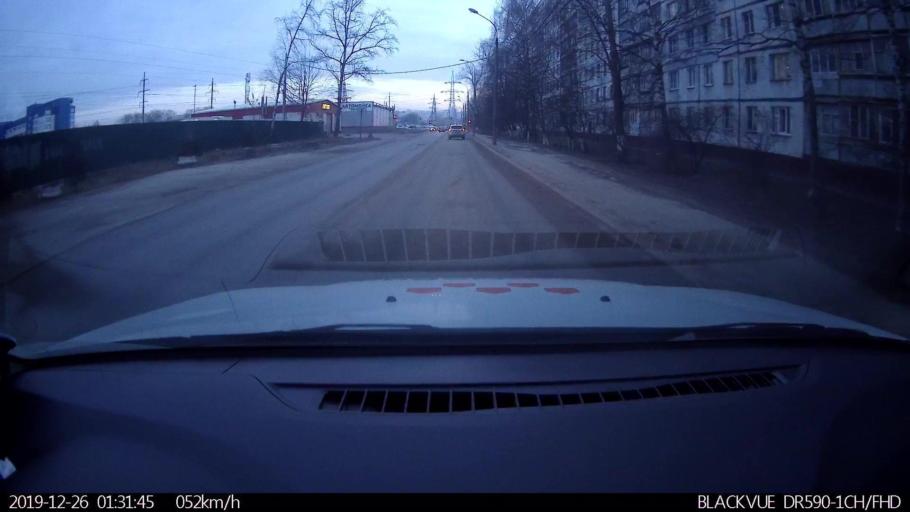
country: RU
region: Nizjnij Novgorod
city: Nizhniy Novgorod
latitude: 56.2654
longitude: 43.9014
